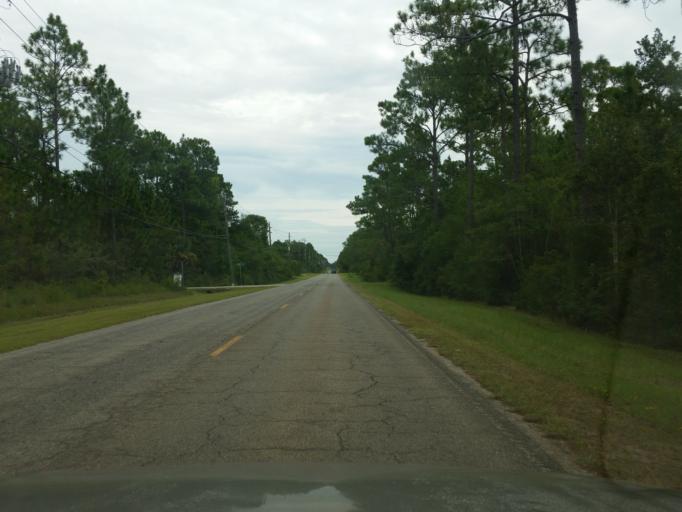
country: US
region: Florida
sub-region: Santa Rosa County
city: Pace
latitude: 30.5442
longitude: -87.0970
